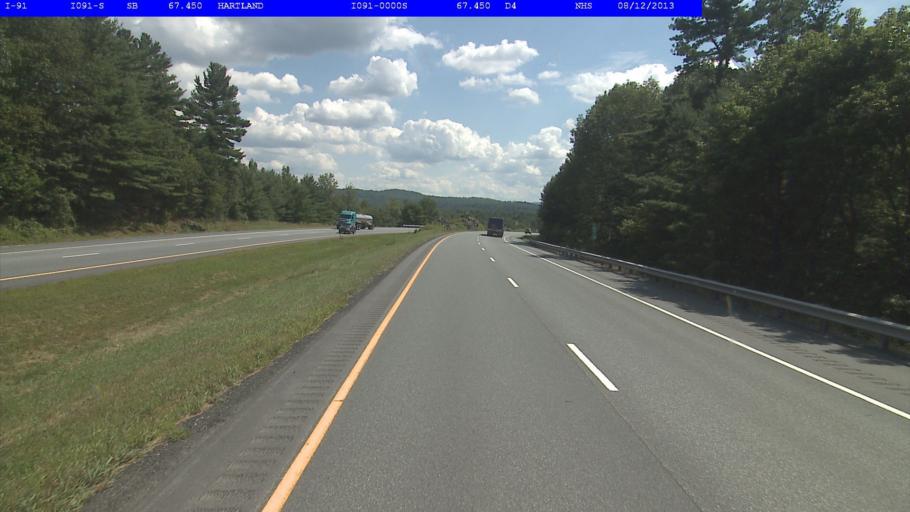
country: US
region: Vermont
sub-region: Windsor County
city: White River Junction
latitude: 43.6079
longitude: -72.3426
